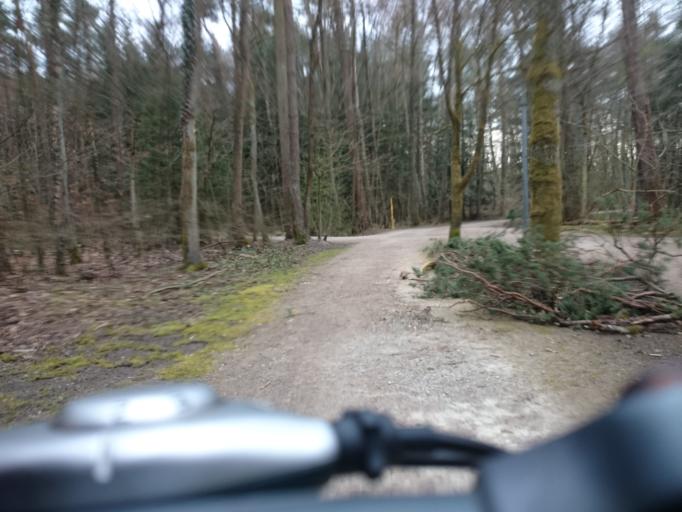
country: DE
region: Bavaria
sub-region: Regierungsbezirk Mittelfranken
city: Nuernberg
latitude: 49.4402
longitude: 11.1356
